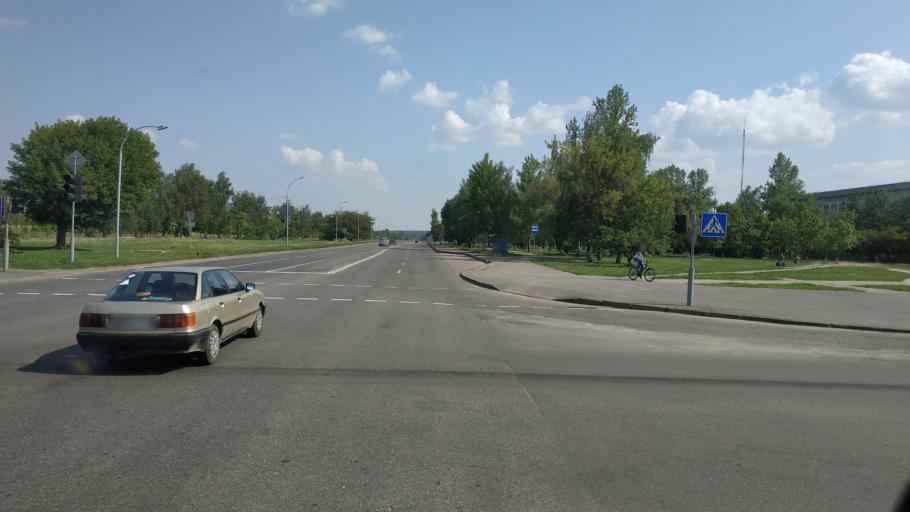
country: BY
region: Mogilev
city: Buynichy
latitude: 53.8664
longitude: 30.3155
